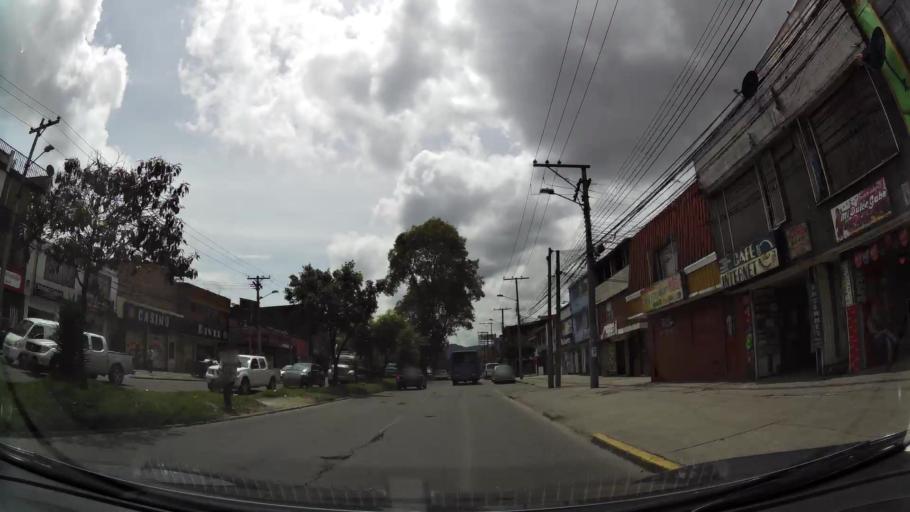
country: CO
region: Cundinamarca
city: Funza
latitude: 4.7034
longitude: -74.1160
